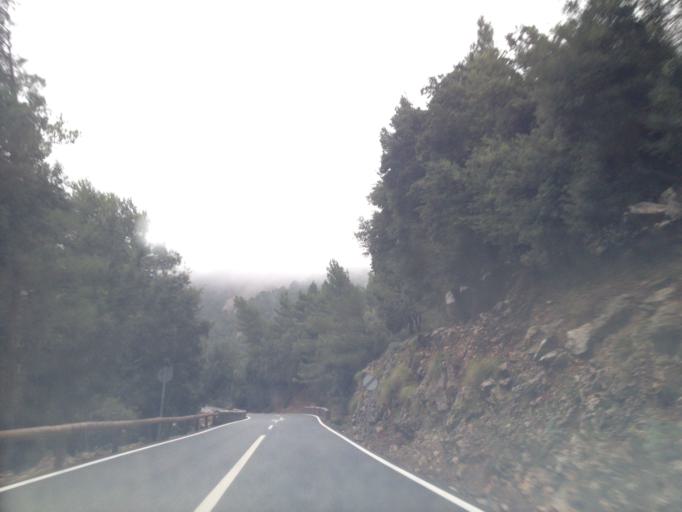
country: ES
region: Balearic Islands
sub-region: Illes Balears
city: Fornalutx
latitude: 39.7916
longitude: 2.7751
